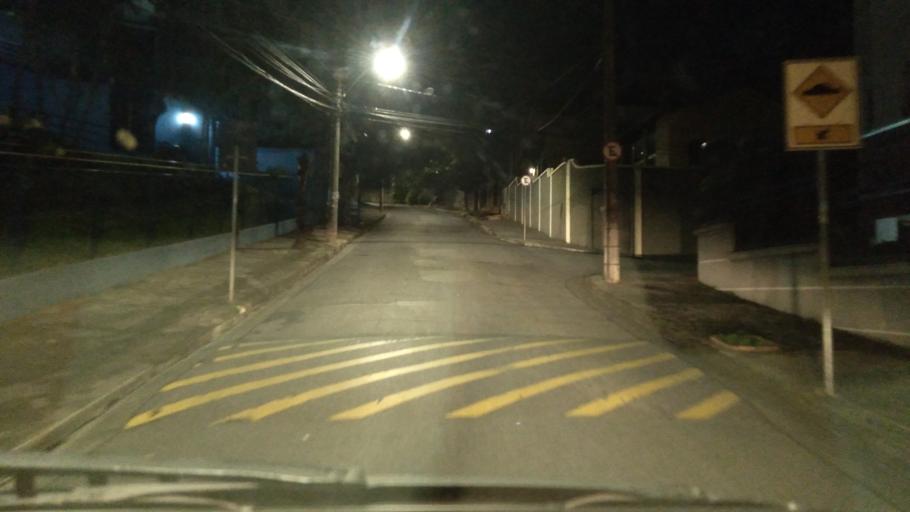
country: BR
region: Minas Gerais
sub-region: Belo Horizonte
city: Belo Horizonte
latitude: -19.8705
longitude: -43.9318
